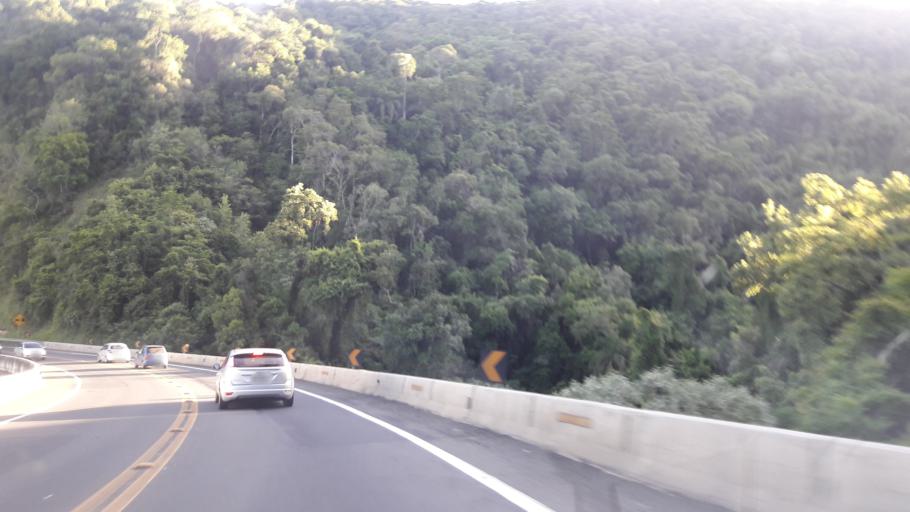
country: BR
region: Parana
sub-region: Prudentopolis
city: Prudentopolis
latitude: -25.3225
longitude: -51.1968
